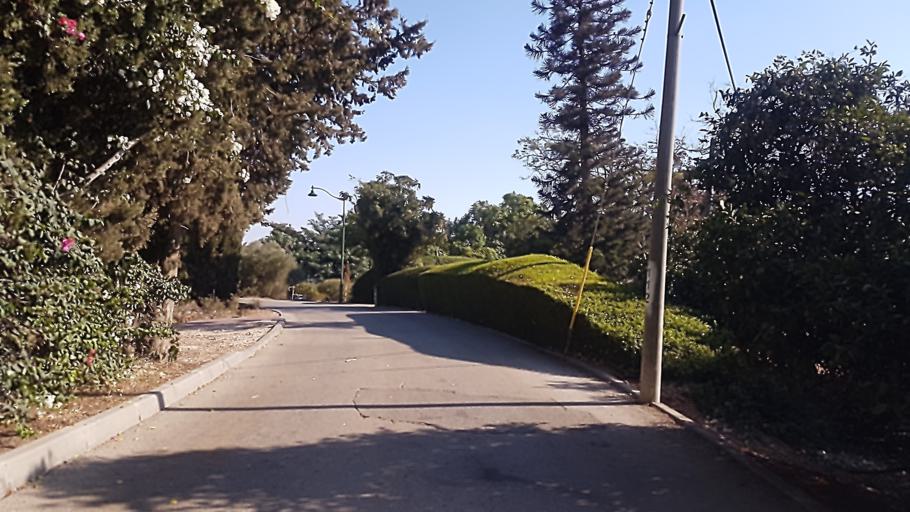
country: IL
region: Central District
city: Kfar Saba
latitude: 32.2027
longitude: 34.9088
